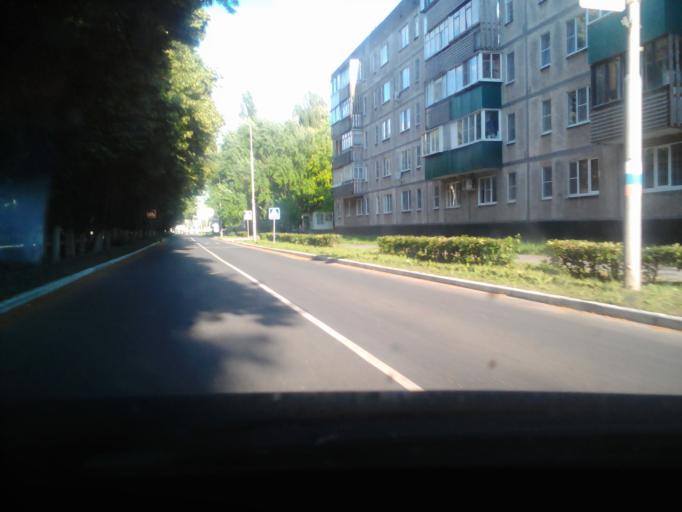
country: RU
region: Kursk
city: Kurchatov
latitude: 51.6603
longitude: 35.6527
